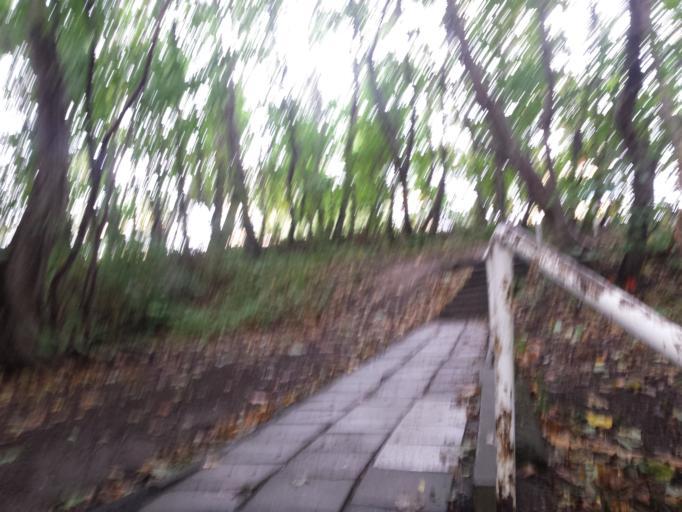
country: DE
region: Mecklenburg-Vorpommern
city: Sassnitz
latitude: 54.5189
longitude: 13.6617
